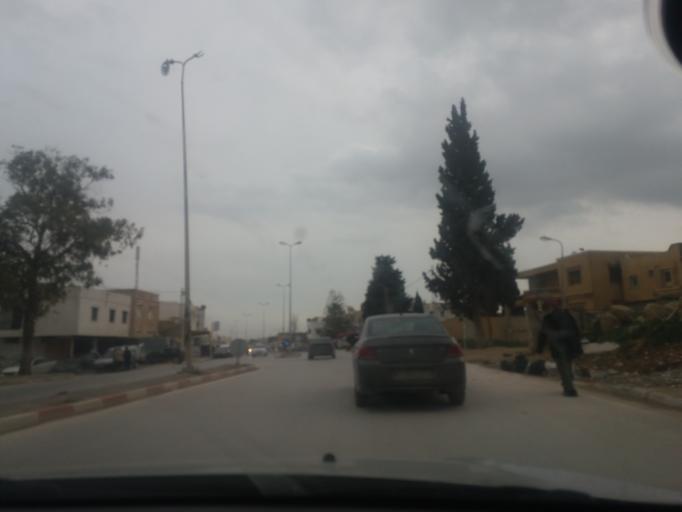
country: TN
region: Ariana
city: Ariana
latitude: 36.8730
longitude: 10.1814
